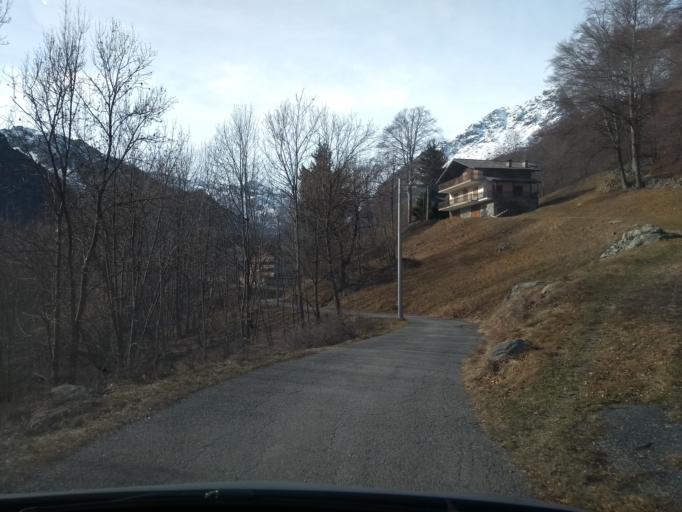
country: IT
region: Piedmont
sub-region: Provincia di Torino
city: Ala di Stura
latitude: 45.3177
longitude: 7.2847
